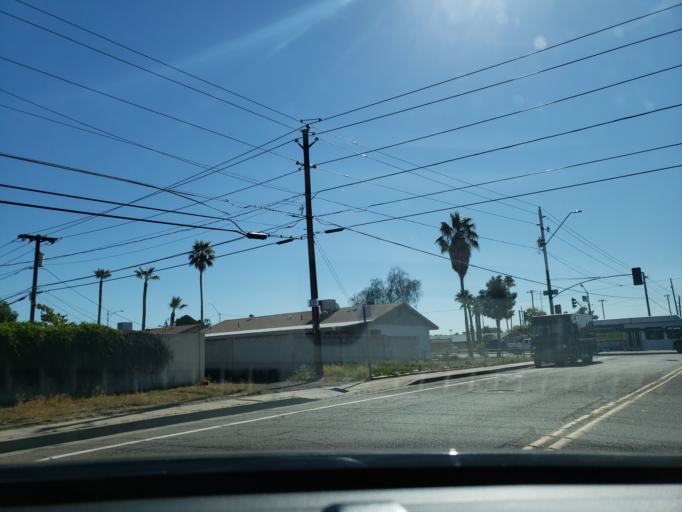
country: US
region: Arizona
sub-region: Maricopa County
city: Glendale
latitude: 33.5970
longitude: -112.1254
